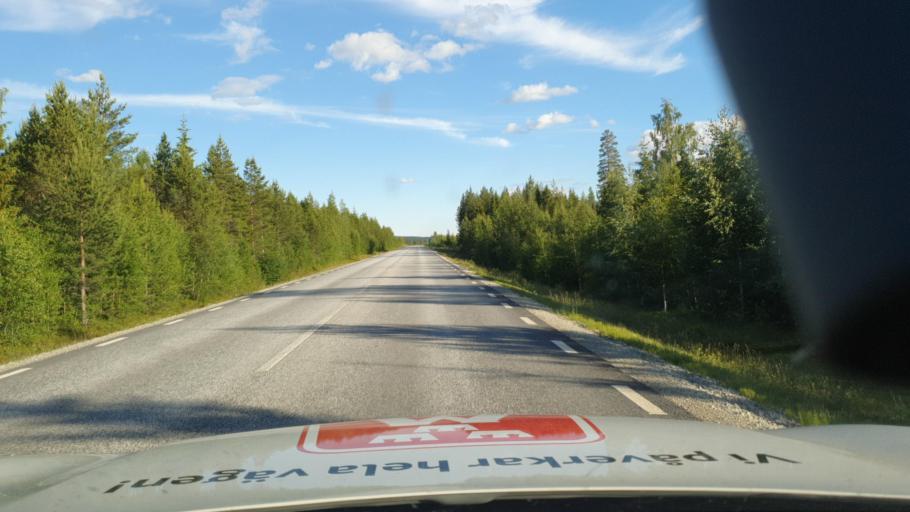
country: SE
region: Vaesterbotten
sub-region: Vindelns Kommun
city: Vindeln
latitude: 64.0702
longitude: 19.6357
